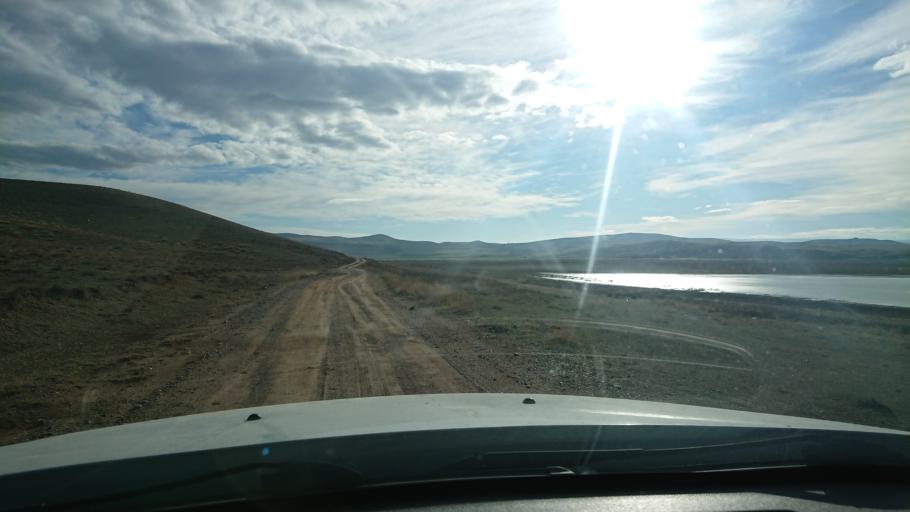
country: TR
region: Aksaray
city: Sariyahsi
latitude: 39.0442
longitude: 33.9713
